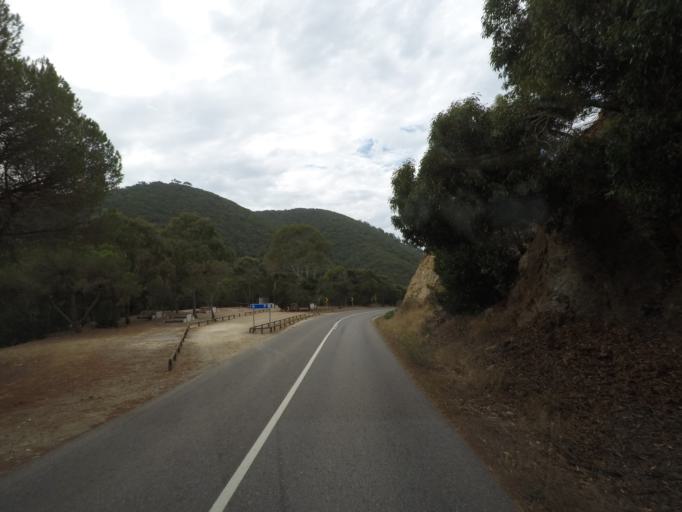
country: PT
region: Faro
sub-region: Aljezur
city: Aljezur
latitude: 37.2031
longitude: -8.8423
